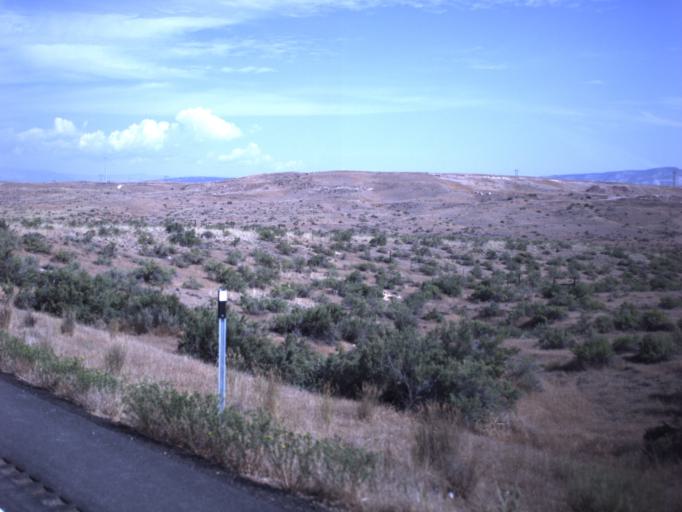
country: US
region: Utah
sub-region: Uintah County
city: Naples
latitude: 40.3610
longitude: -109.3179
